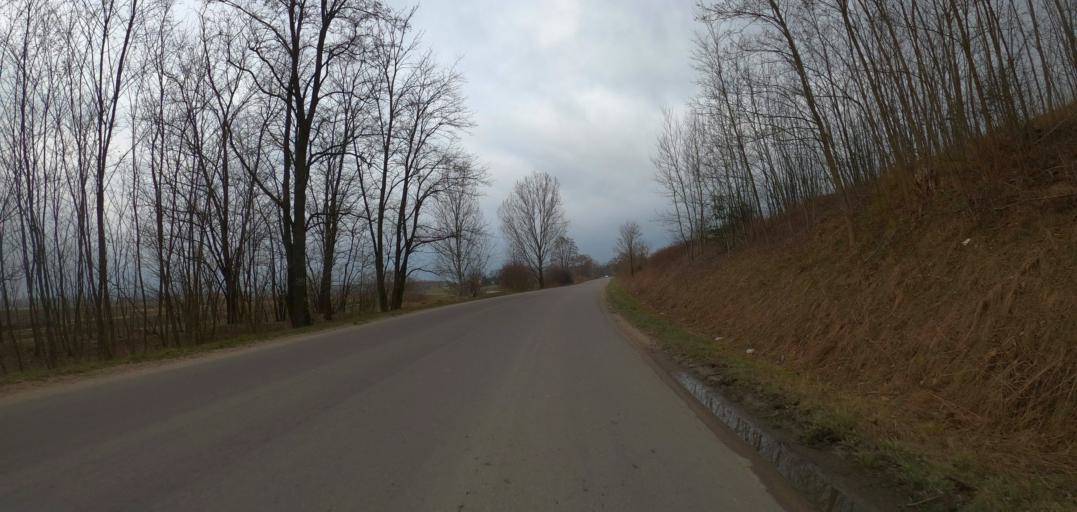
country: PL
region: Subcarpathian Voivodeship
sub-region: Powiat debicki
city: Pilzno
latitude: 49.9819
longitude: 21.3292
